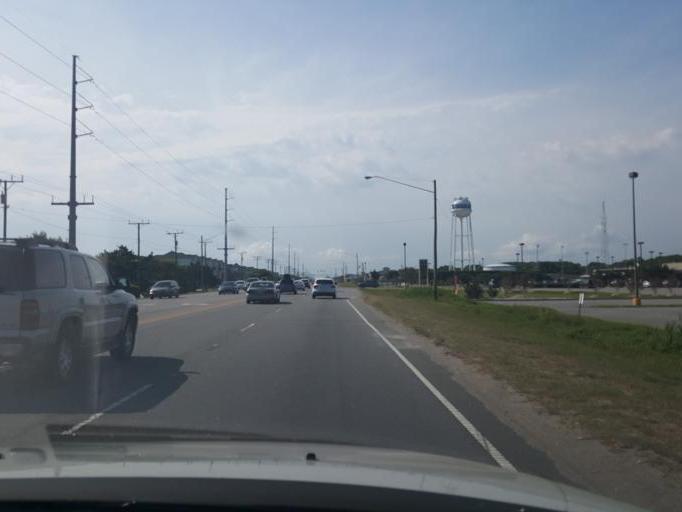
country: US
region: North Carolina
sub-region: Dare County
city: Kill Devil Hills
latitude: 36.0335
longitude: -75.6730
